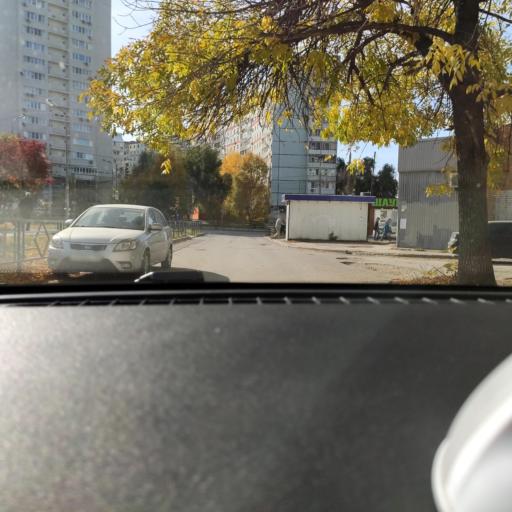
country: RU
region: Samara
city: Samara
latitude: 53.2638
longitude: 50.2223
